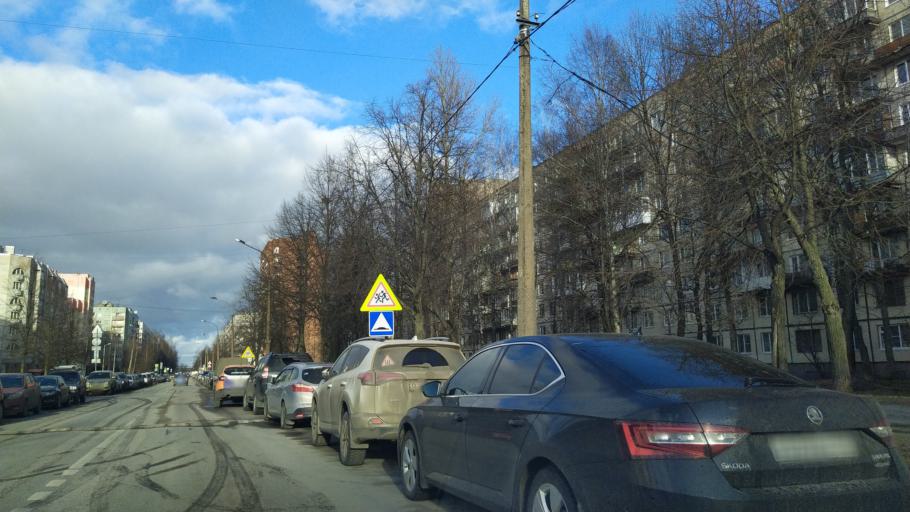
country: RU
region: Leningrad
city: Parnas
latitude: 60.0480
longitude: 30.3679
